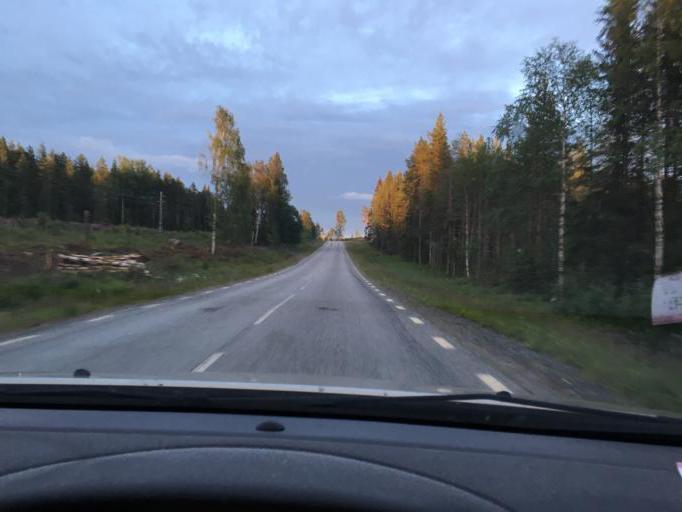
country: SE
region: Norrbotten
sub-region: Lulea Kommun
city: Ranea
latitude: 66.0510
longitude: 22.3887
